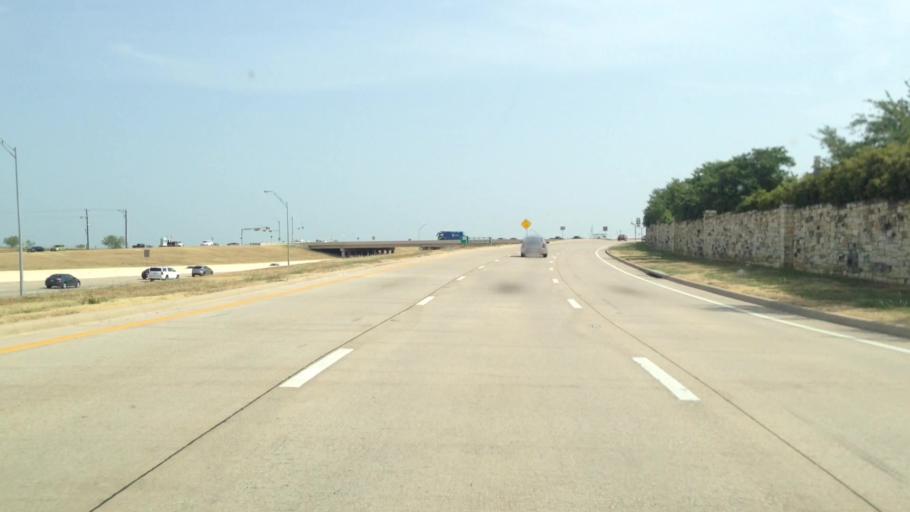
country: US
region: Texas
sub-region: Denton County
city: The Colony
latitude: 33.0436
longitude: -96.9224
